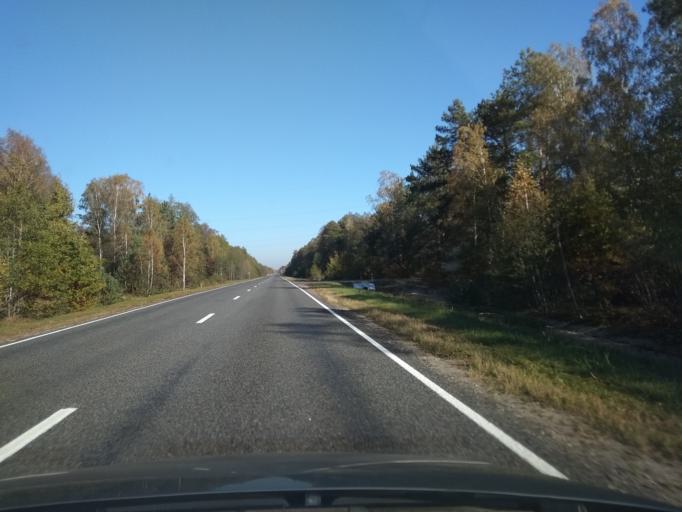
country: BY
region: Brest
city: Malaryta
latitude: 51.9763
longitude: 24.2005
